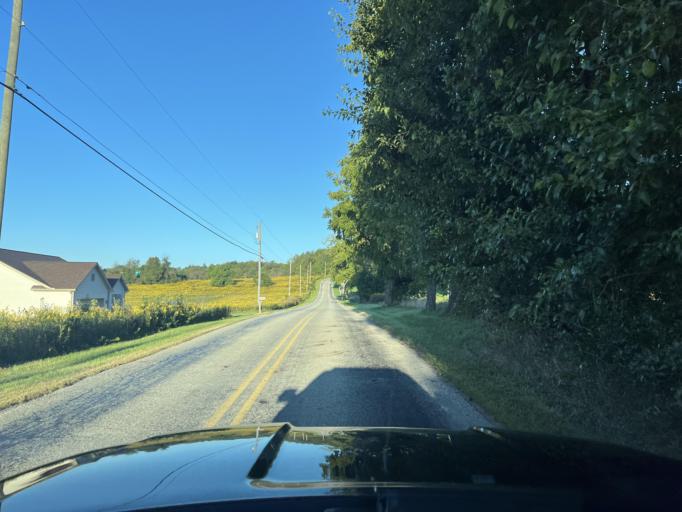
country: US
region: Pennsylvania
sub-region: Fayette County
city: Leith-Hatfield
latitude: 39.8685
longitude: -79.7338
